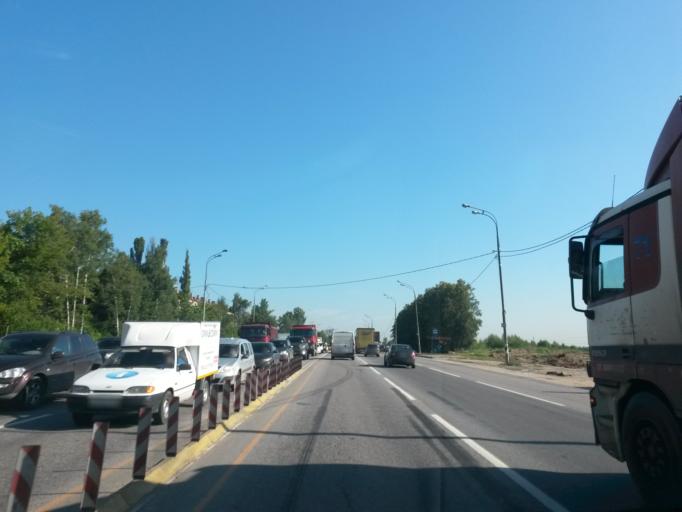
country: RU
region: Moskovskaya
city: Bolshevo
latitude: 55.9472
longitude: 37.8146
